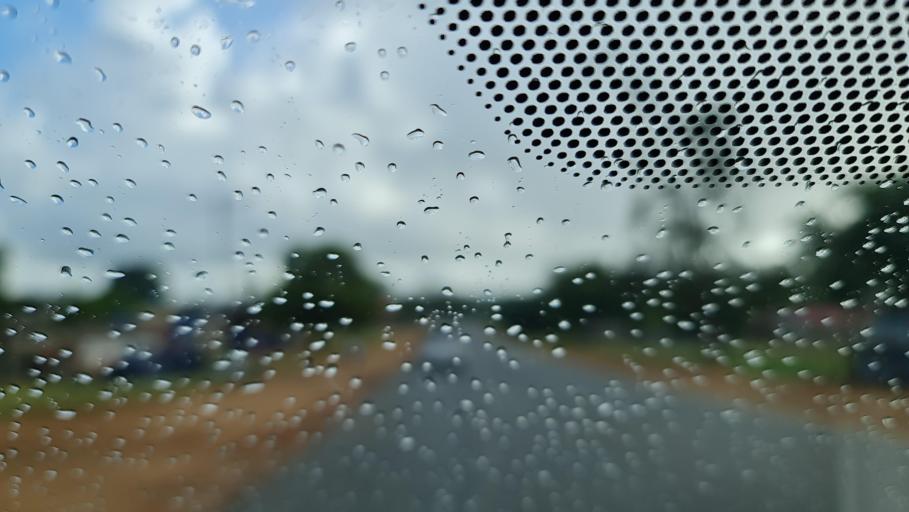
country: MZ
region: Gaza
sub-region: Xai-Xai District
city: Xai-Xai
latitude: -25.0337
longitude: 33.7233
